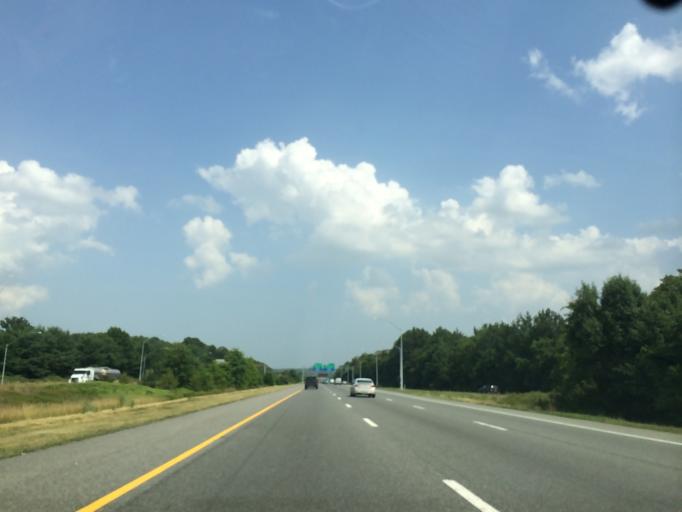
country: US
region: Maryland
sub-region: Howard County
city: Riverside
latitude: 39.1805
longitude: -76.8718
